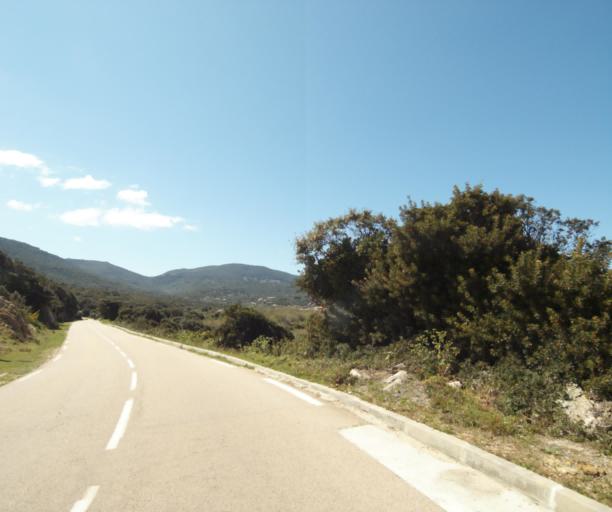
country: FR
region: Corsica
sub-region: Departement de la Corse-du-Sud
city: Propriano
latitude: 41.6517
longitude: 8.8808
